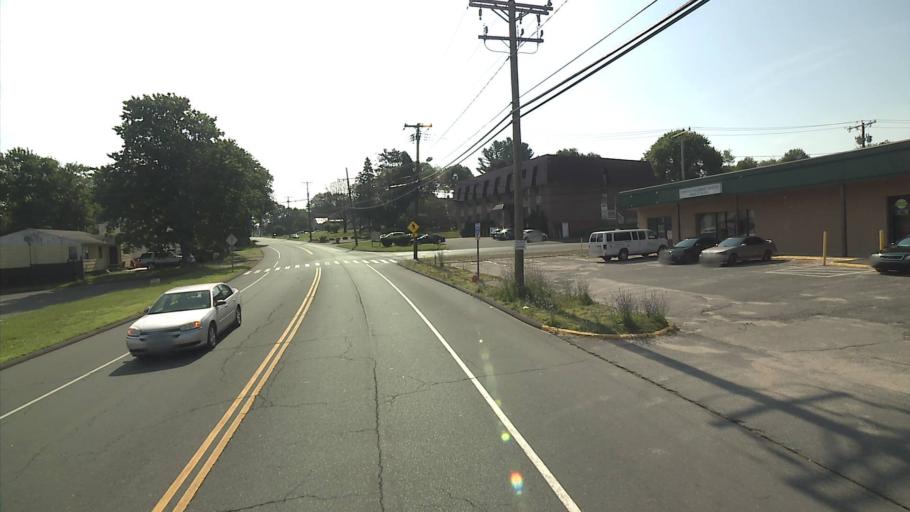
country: US
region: Connecticut
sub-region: New Haven County
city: Wolcott
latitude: 41.5521
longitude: -72.9867
